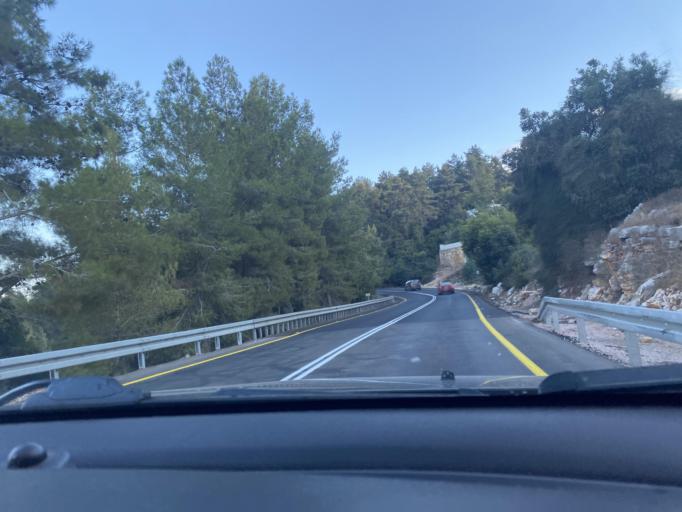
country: IL
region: Northern District
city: Kefar Weradim
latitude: 32.9989
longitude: 35.2821
